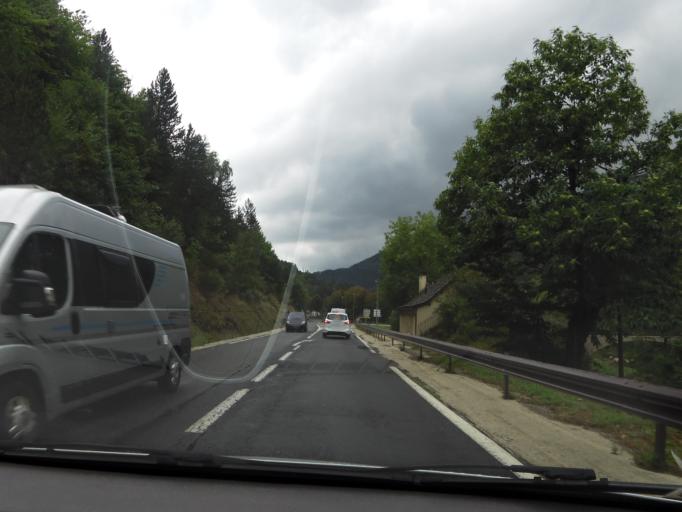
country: FR
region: Languedoc-Roussillon
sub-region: Departement de la Lozere
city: Florac
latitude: 44.3198
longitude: 3.6005
